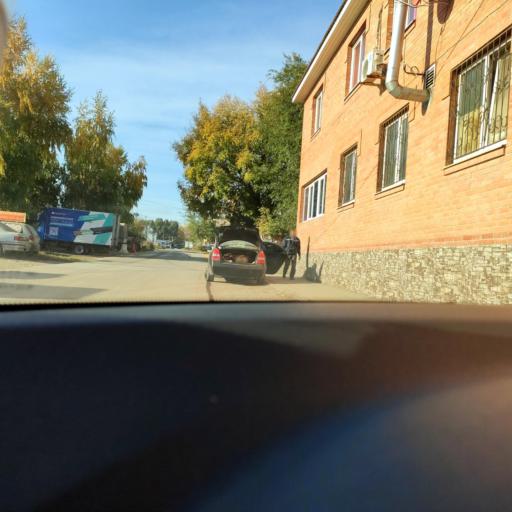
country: RU
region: Samara
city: Samara
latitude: 53.2199
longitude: 50.2173
